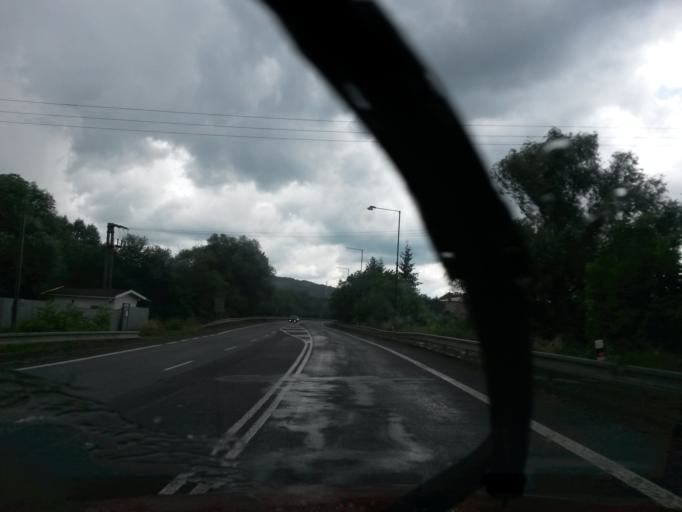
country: SK
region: Presovsky
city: Vranov nad Topl'ou
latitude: 48.8540
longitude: 21.7458
